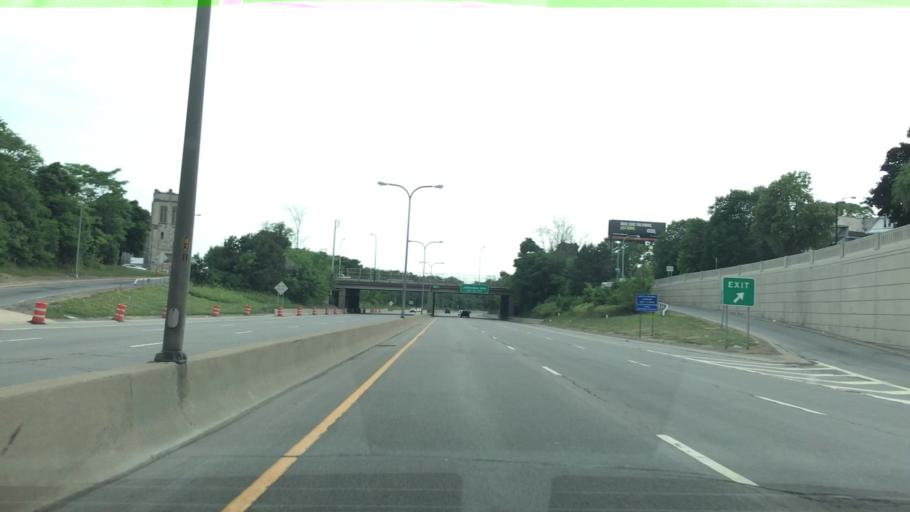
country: US
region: New York
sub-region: Erie County
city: Buffalo
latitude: 42.9053
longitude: -78.8451
